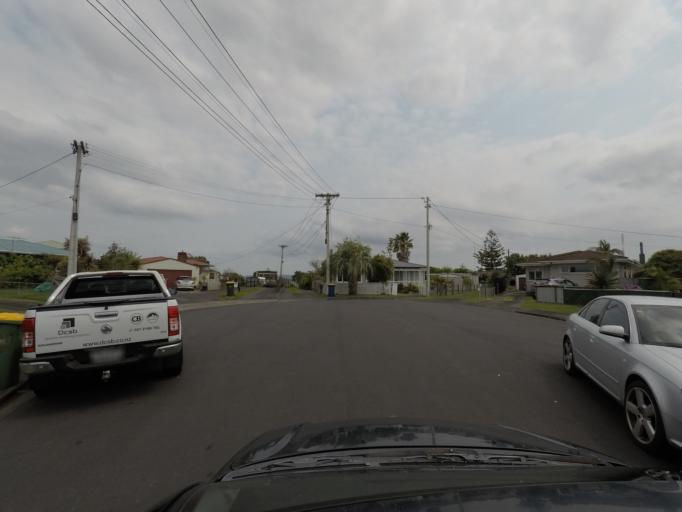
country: NZ
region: Auckland
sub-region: Auckland
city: Rosebank
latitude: -36.8409
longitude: 174.6410
